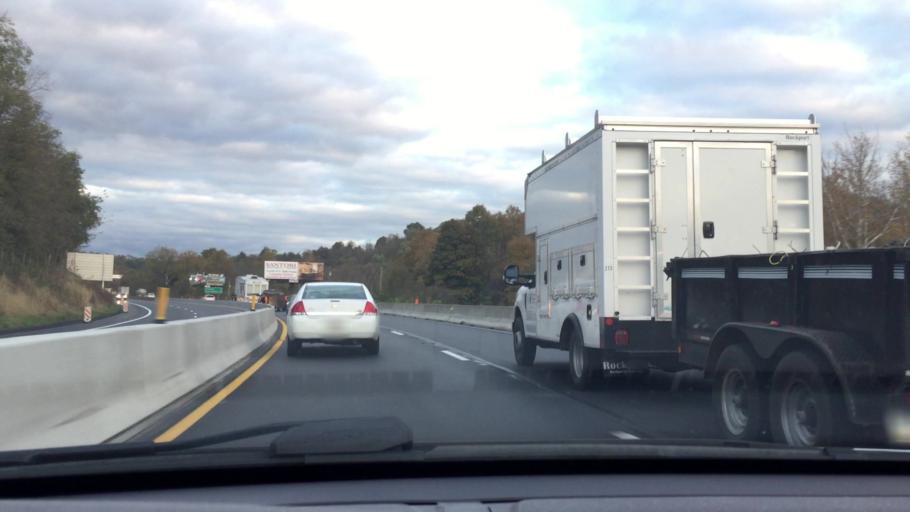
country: US
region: Pennsylvania
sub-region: Washington County
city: Bentleyville
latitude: 40.1301
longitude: -79.9880
